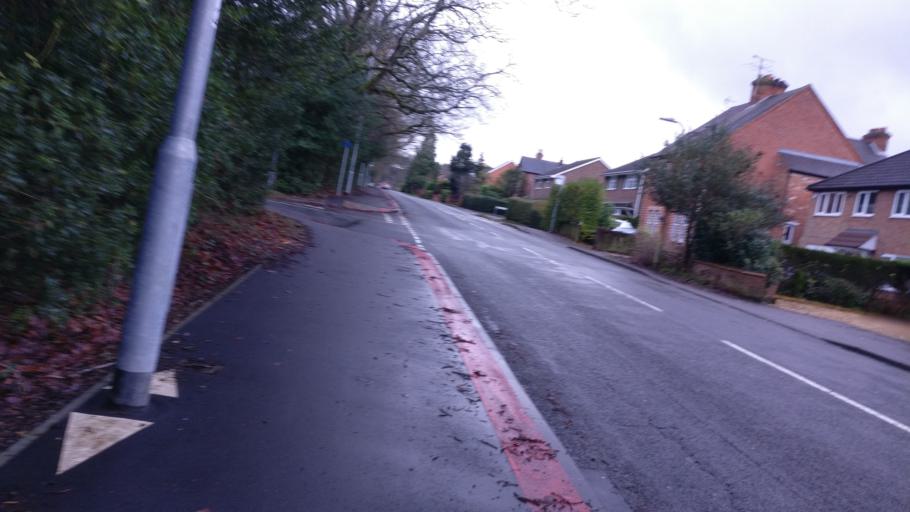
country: GB
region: England
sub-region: Bracknell Forest
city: Crowthorne
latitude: 51.3755
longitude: -0.7900
